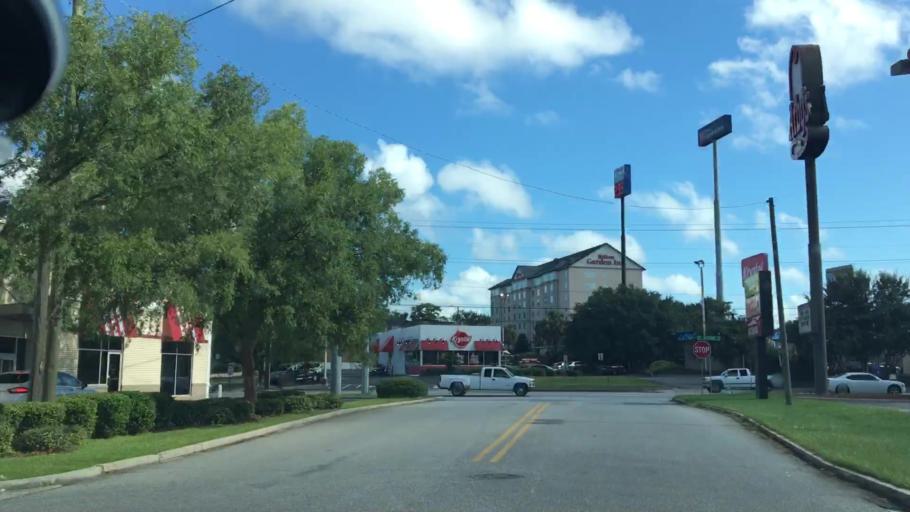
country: US
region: Georgia
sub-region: Lowndes County
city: Remerton
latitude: 30.8418
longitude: -83.3261
